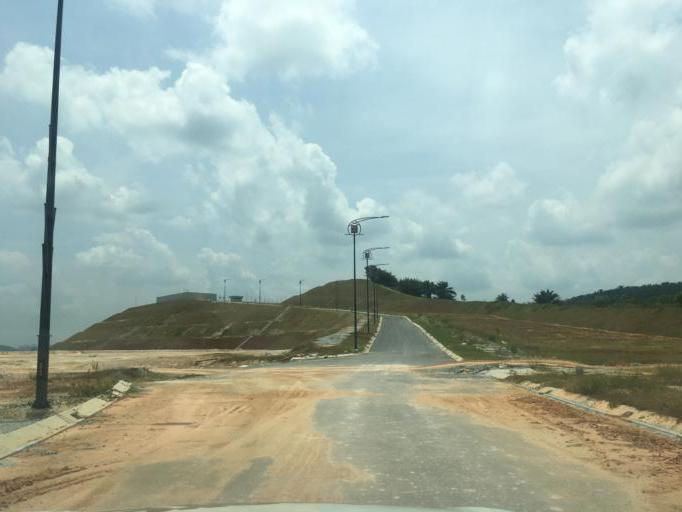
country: MY
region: Putrajaya
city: Putrajaya
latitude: 2.8463
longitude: 101.7108
